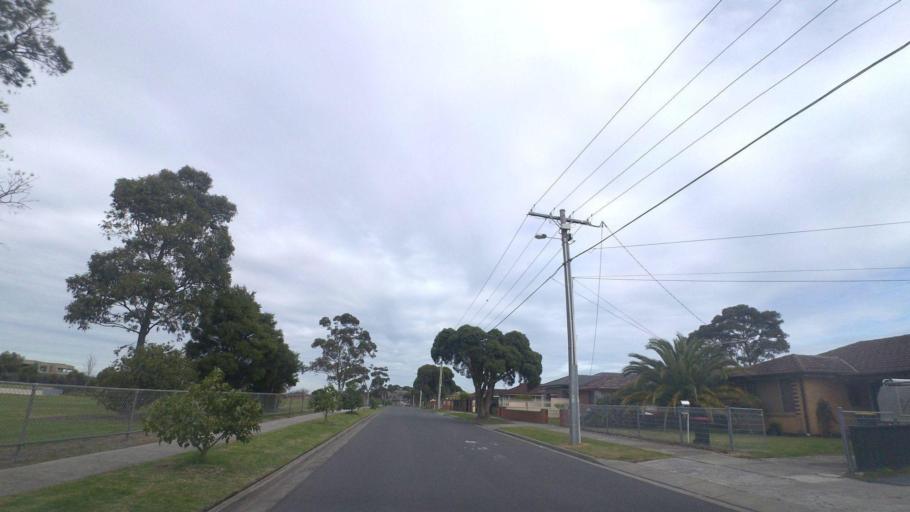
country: AU
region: Victoria
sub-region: Kingston
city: Clayton South
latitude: -37.9402
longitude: 145.1342
